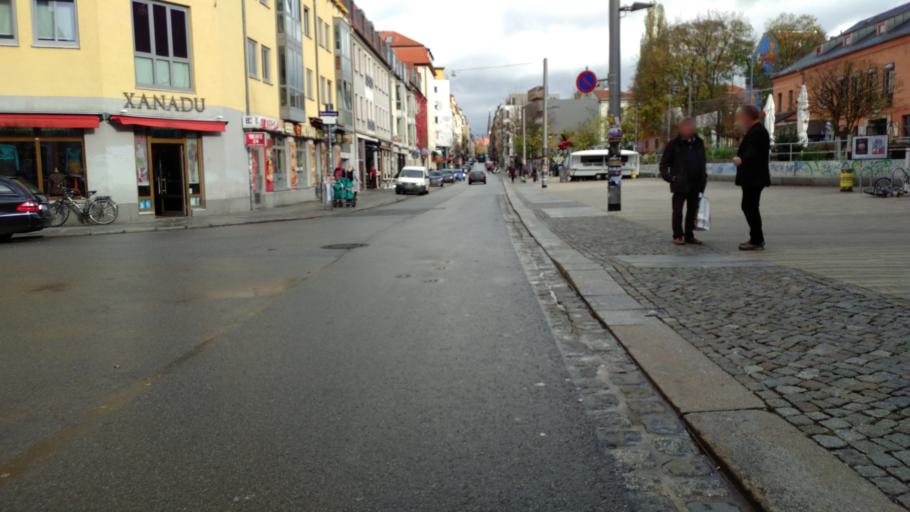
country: DE
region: Saxony
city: Dresden
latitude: 51.0661
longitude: 13.7507
